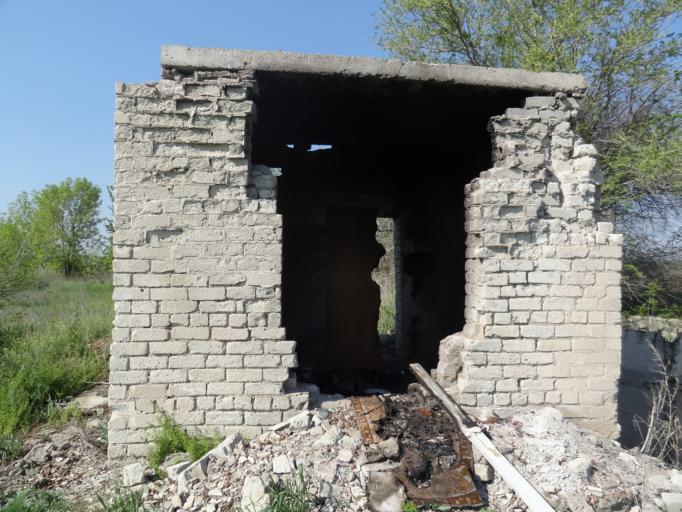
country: RU
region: Saratov
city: Engel's
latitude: 51.4227
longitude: 46.1185
